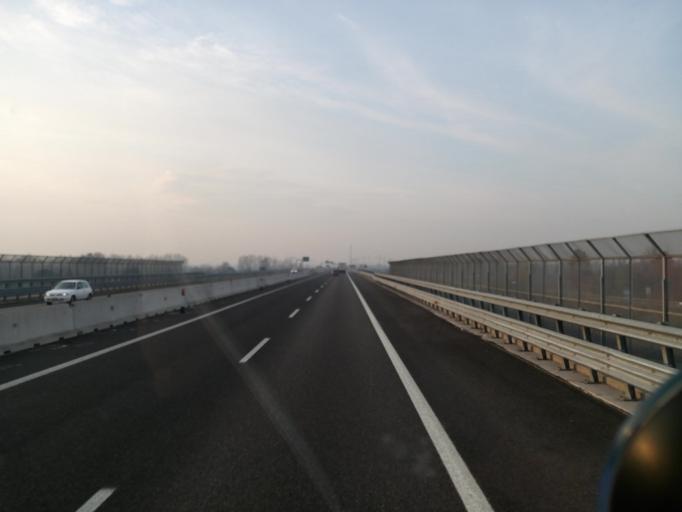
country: IT
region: Lombardy
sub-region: Provincia di Brescia
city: Montirone
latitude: 45.4650
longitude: 10.2150
